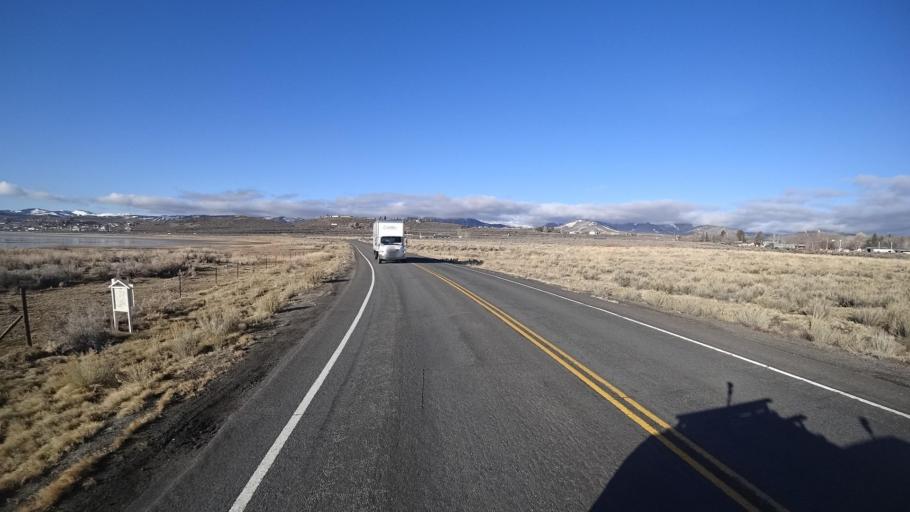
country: US
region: Nevada
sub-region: Washoe County
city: Cold Springs
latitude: 39.6711
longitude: -119.9903
